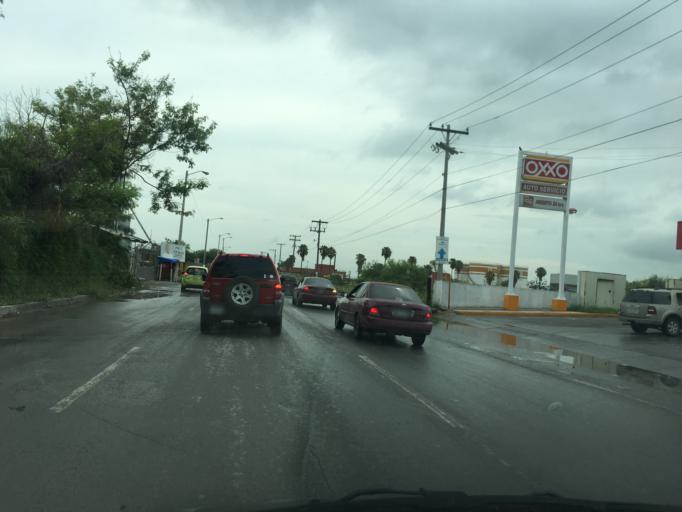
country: MX
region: Tamaulipas
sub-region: Matamoros
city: Heroica Matamoros
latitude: 25.8776
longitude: -97.5280
